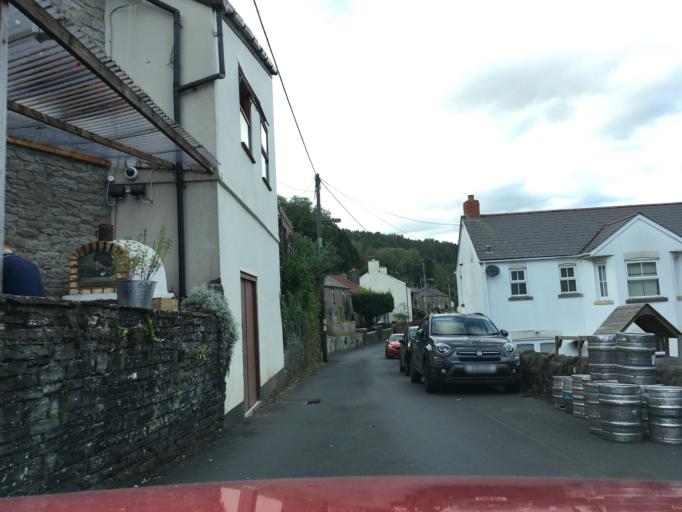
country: GB
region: Wales
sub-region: Cardiff
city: Pentyrch
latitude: 51.5474
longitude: -3.2768
